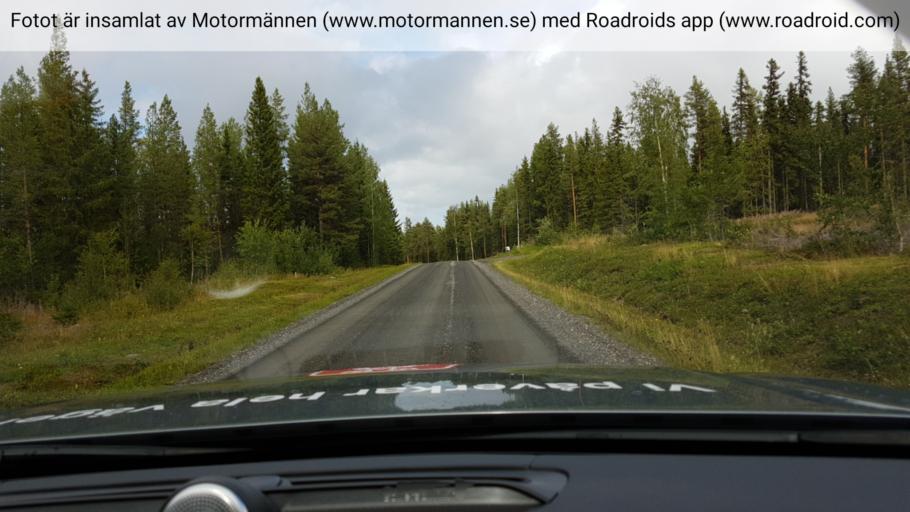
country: SE
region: Jaemtland
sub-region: OEstersunds Kommun
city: Lit
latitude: 63.7467
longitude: 14.6511
